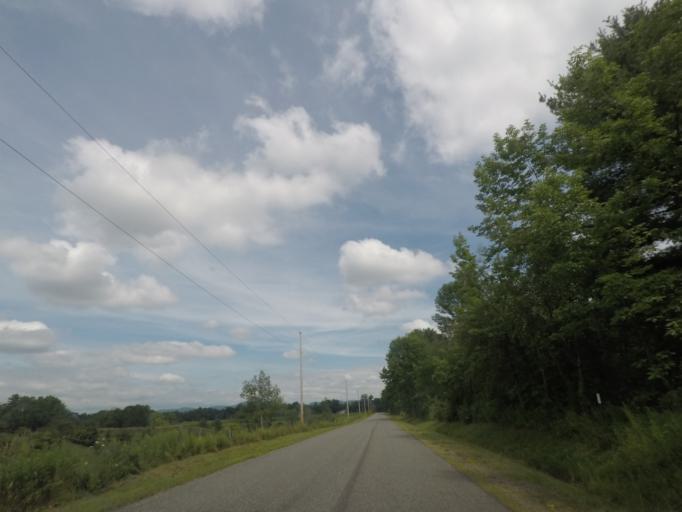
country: US
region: New York
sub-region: Saratoga County
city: Stillwater
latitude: 43.0107
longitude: -73.6339
